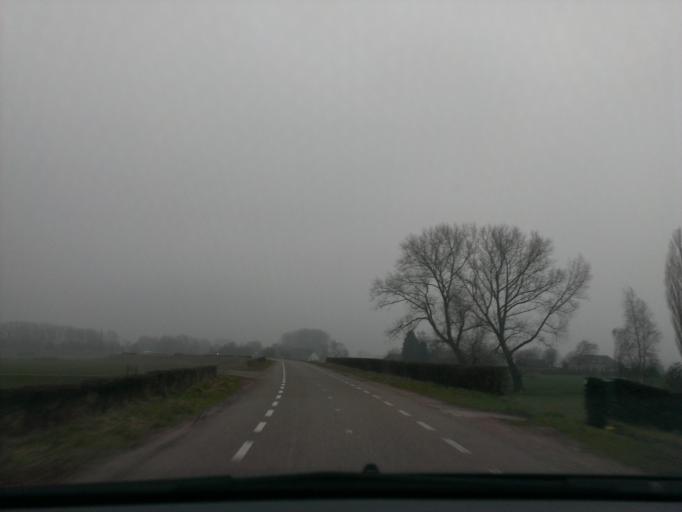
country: NL
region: Overijssel
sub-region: Gemeente Olst-Wijhe
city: Olst
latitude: 52.3055
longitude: 6.0914
